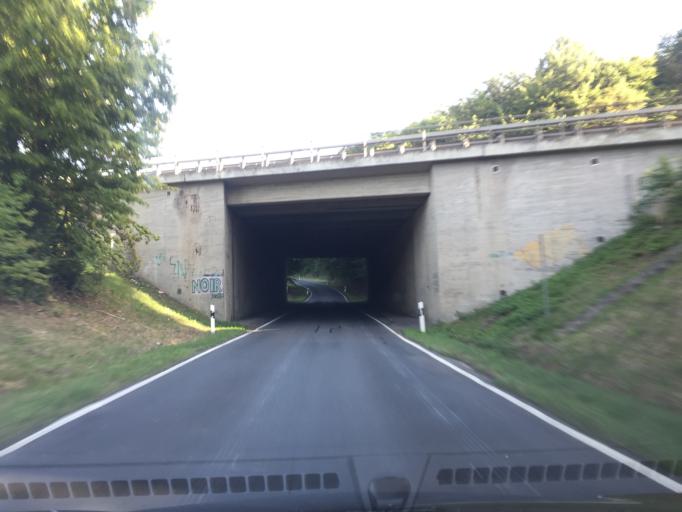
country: DE
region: Rheinland-Pfalz
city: Grossholbach
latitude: 50.4550
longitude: 7.8838
